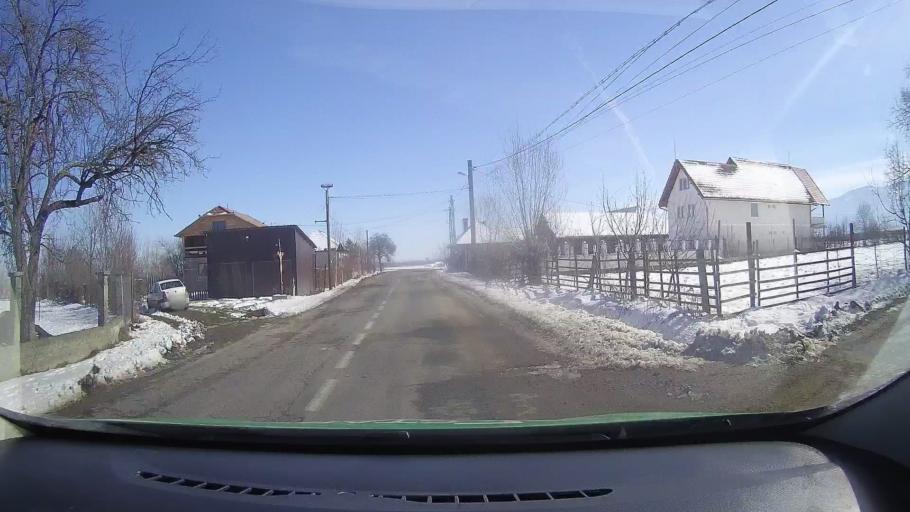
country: RO
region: Brasov
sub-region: Comuna Recea
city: Recea
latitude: 45.7309
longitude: 24.9489
